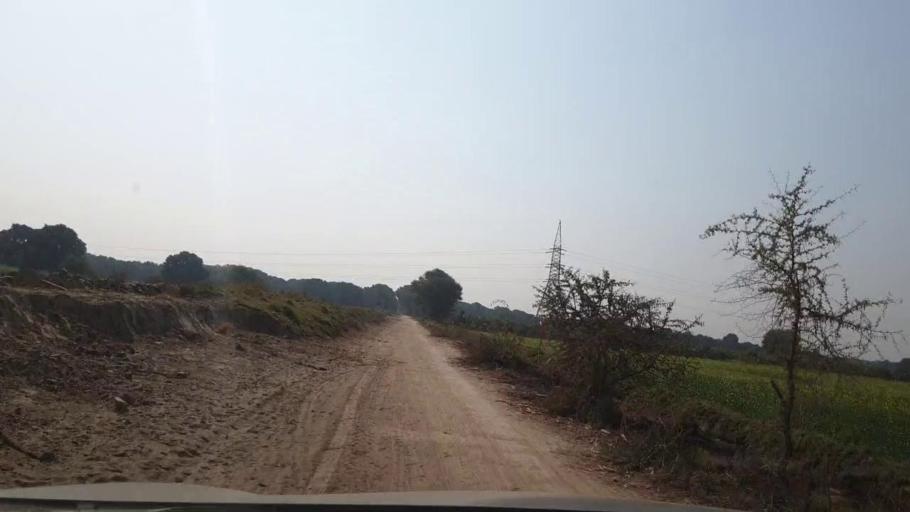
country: PK
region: Sindh
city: Tando Allahyar
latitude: 25.5003
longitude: 68.7860
